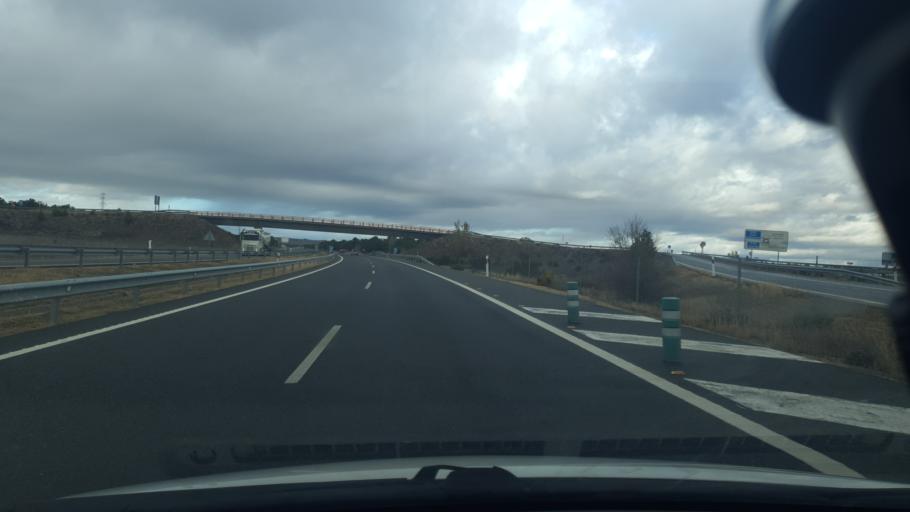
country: ES
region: Castille and Leon
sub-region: Provincia de Segovia
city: Sanchonuno
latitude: 41.3403
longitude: -4.3031
